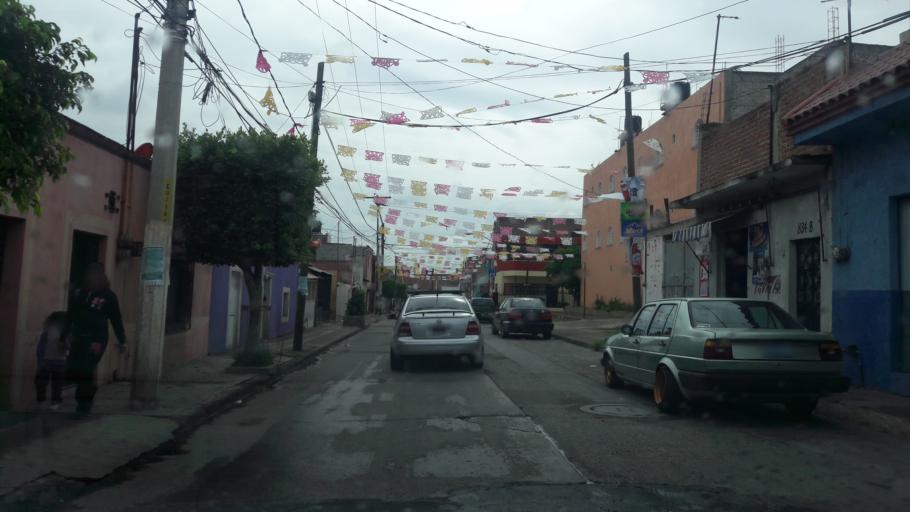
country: MX
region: Guanajuato
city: Leon
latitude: 21.1149
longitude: -101.6910
